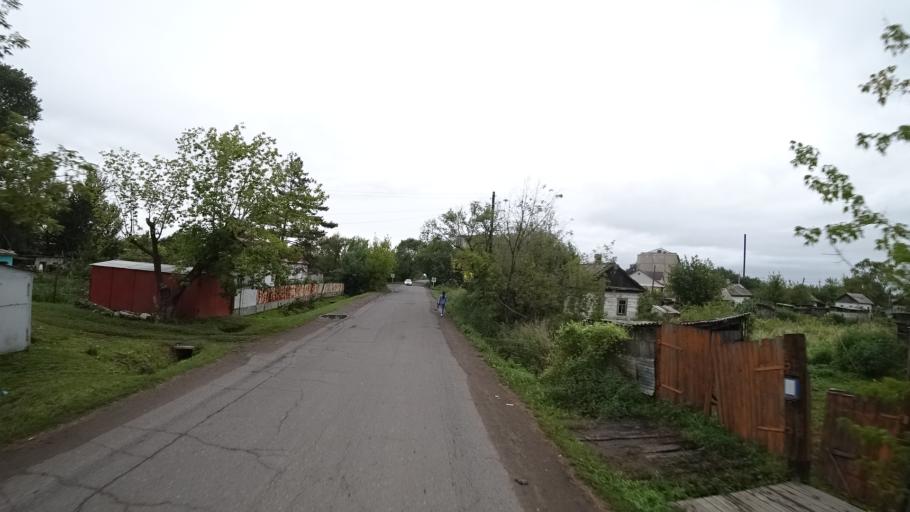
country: RU
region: Primorskiy
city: Chernigovka
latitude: 44.3338
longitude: 132.5319
